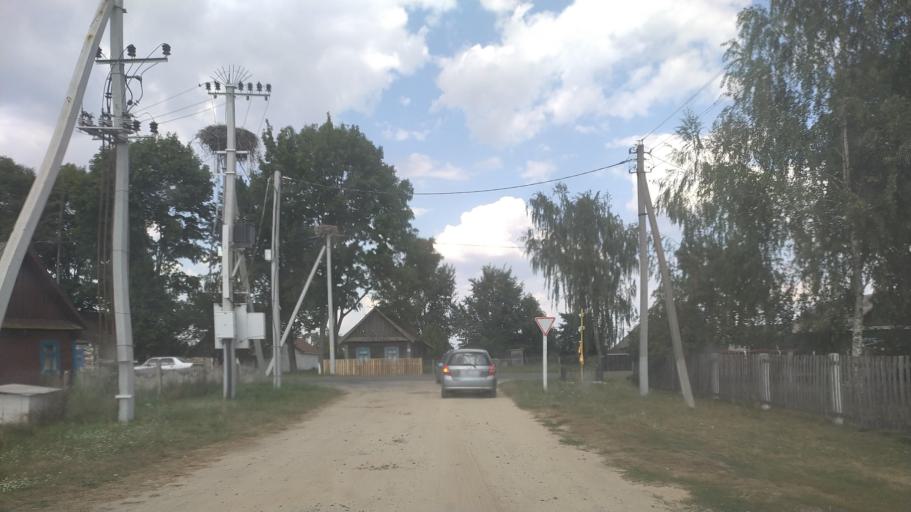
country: BY
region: Brest
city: Drahichyn
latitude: 52.1013
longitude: 25.1459
